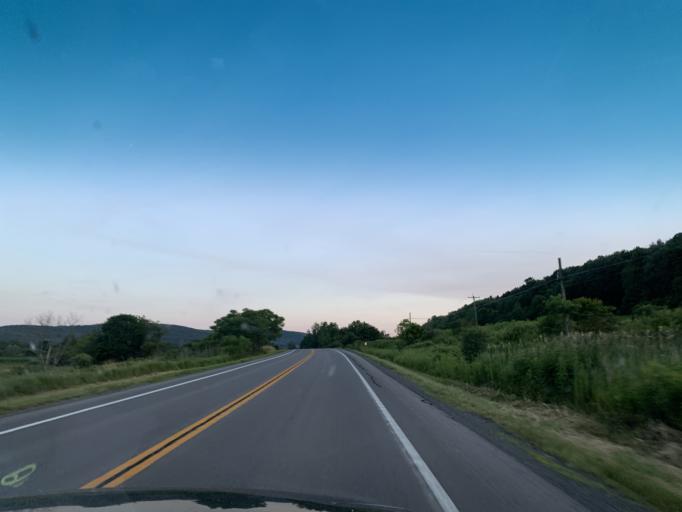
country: US
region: New York
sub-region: Oneida County
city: Waterville
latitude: 42.8028
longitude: -75.2541
